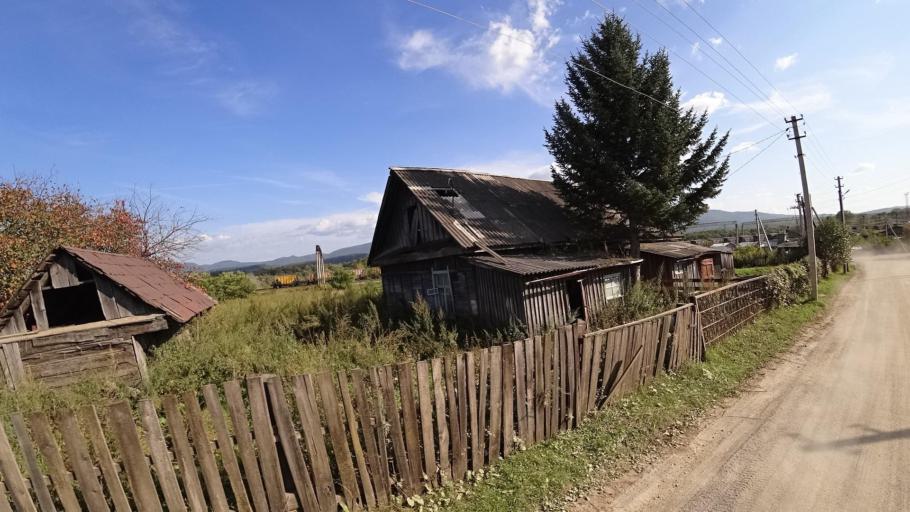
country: RU
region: Jewish Autonomous Oblast
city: Birakan
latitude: 48.9957
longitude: 131.7245
